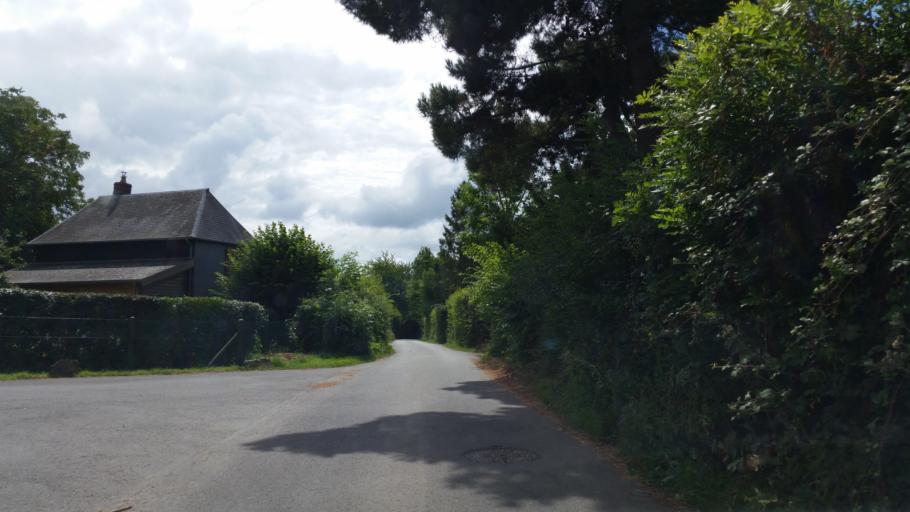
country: FR
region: Lower Normandy
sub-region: Departement du Calvados
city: Equemauville
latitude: 49.3950
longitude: 0.2282
